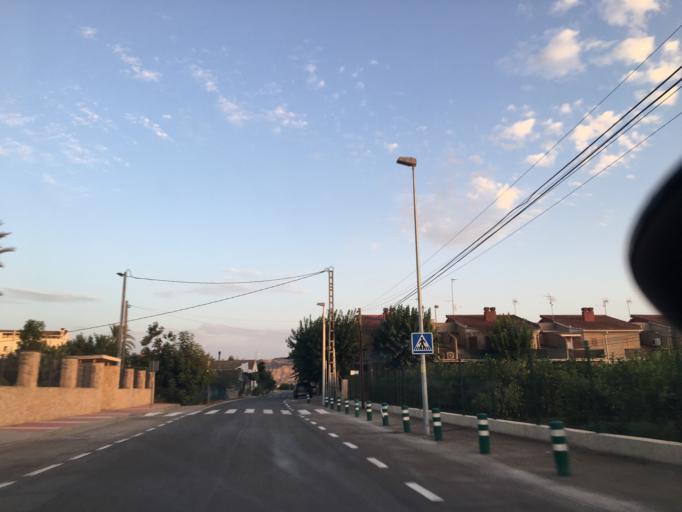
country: ES
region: Murcia
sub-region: Murcia
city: Santomera
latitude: 38.0192
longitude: -1.0522
